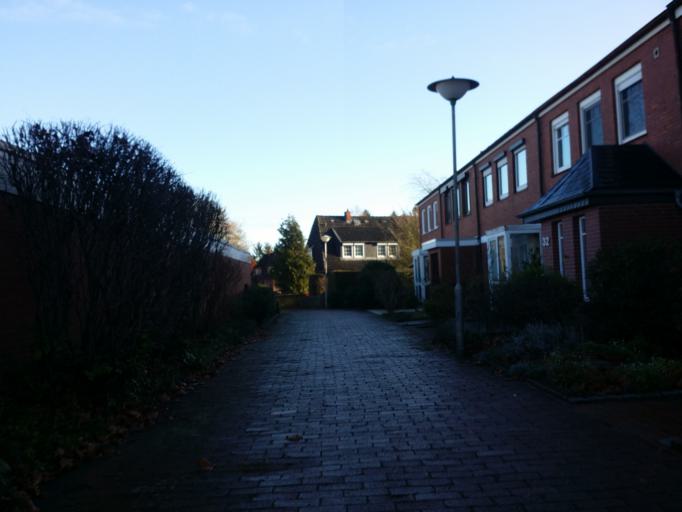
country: DE
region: Lower Saxony
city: Stuhr
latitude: 53.0524
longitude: 8.7625
